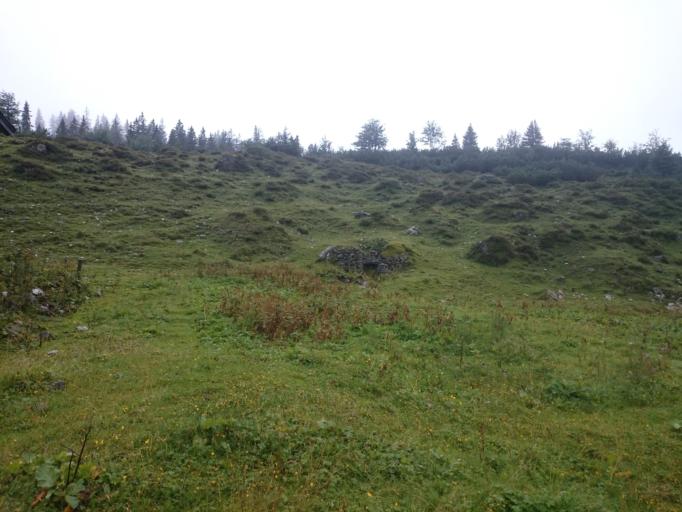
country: AT
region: Tyrol
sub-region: Politischer Bezirk Innsbruck Land
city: Absam
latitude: 47.4093
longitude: 11.4935
